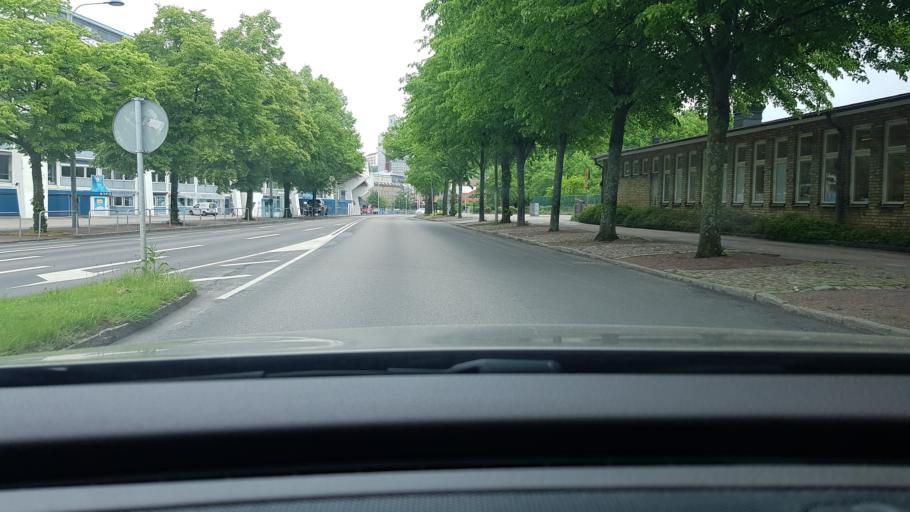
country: SE
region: Vaestra Goetaland
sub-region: Goteborg
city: Goeteborg
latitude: 57.7044
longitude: 11.9857
